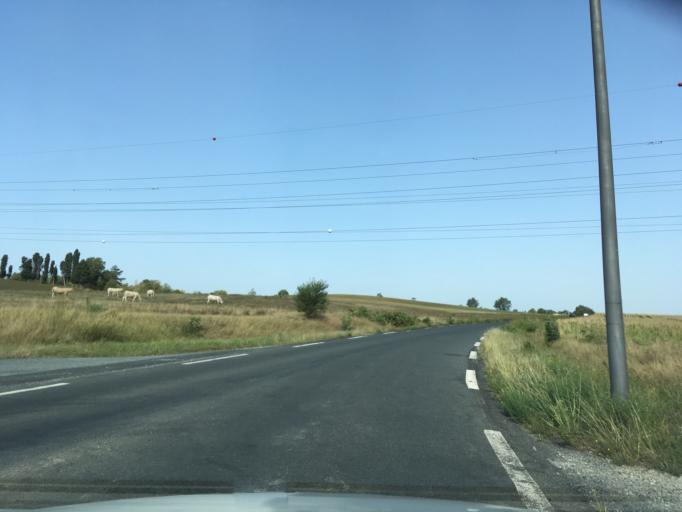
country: FR
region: Midi-Pyrenees
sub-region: Departement du Tarn
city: Lagarrigue
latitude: 43.5791
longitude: 2.2664
